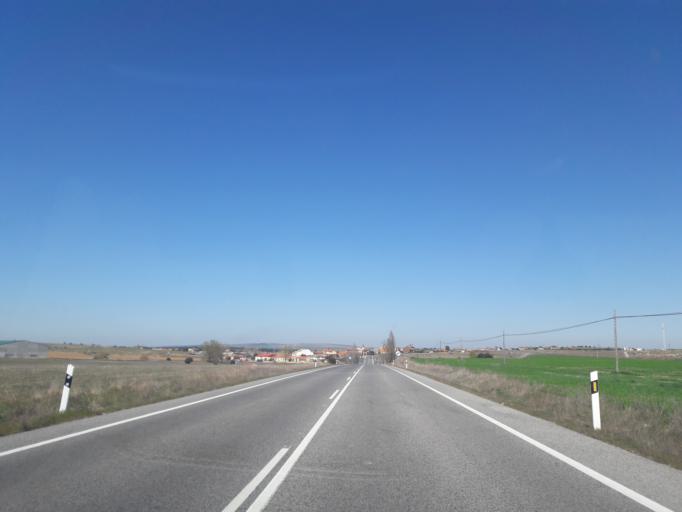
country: ES
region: Castille and Leon
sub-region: Provincia de Salamanca
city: Mozarbez
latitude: 40.8504
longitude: -5.6463
